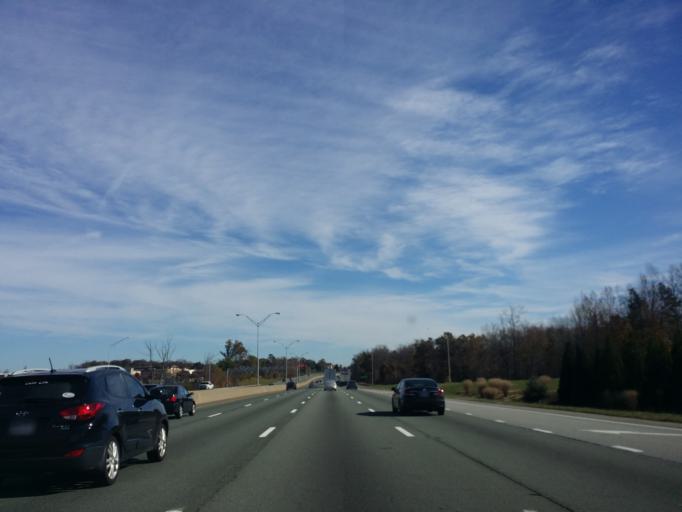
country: US
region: North Carolina
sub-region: Alamance County
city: Elon
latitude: 36.0657
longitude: -79.5141
